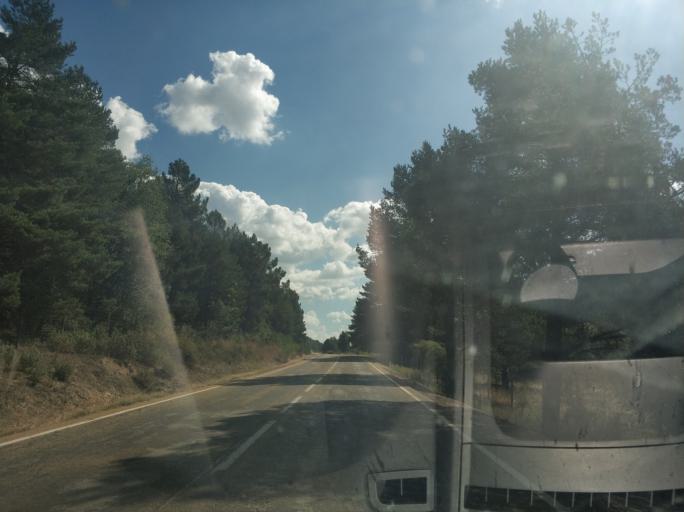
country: ES
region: Castille and Leon
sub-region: Provincia de Soria
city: San Leonardo de Yague
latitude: 41.8132
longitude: -3.0641
